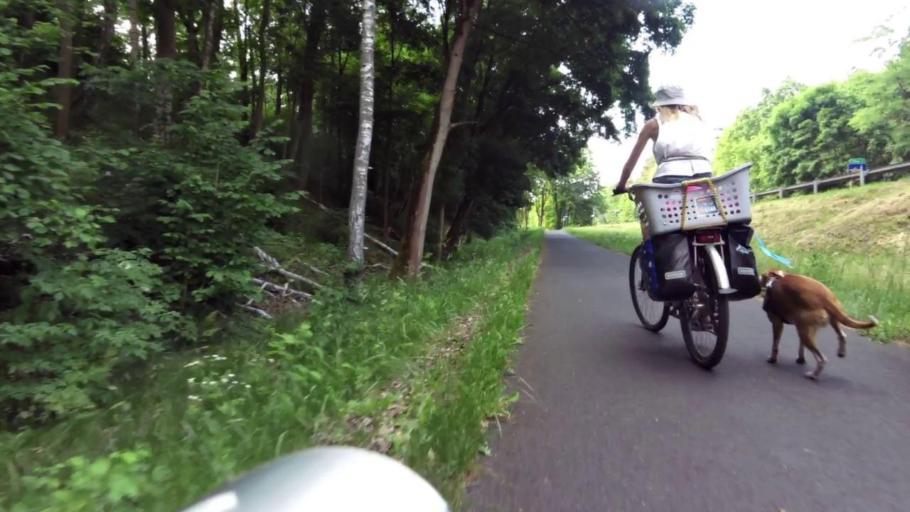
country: PL
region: Kujawsko-Pomorskie
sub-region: Powiat torunski
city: Lysomice
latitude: 53.0808
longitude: 18.5396
